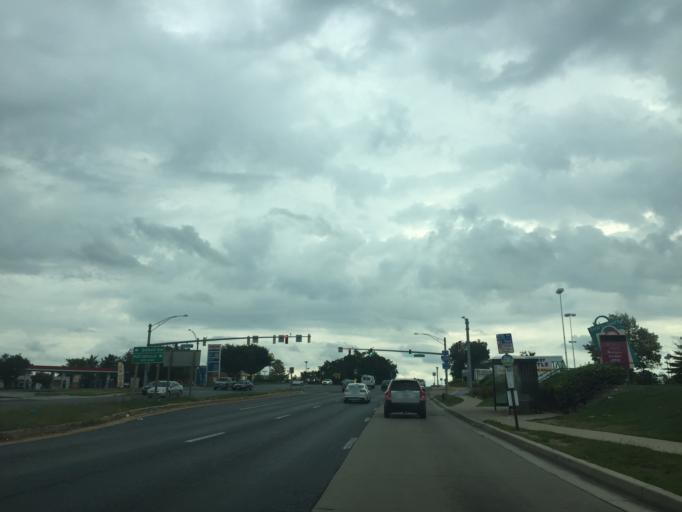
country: US
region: Maryland
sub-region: Baltimore County
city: Woodlawn
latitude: 39.3129
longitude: -76.7513
